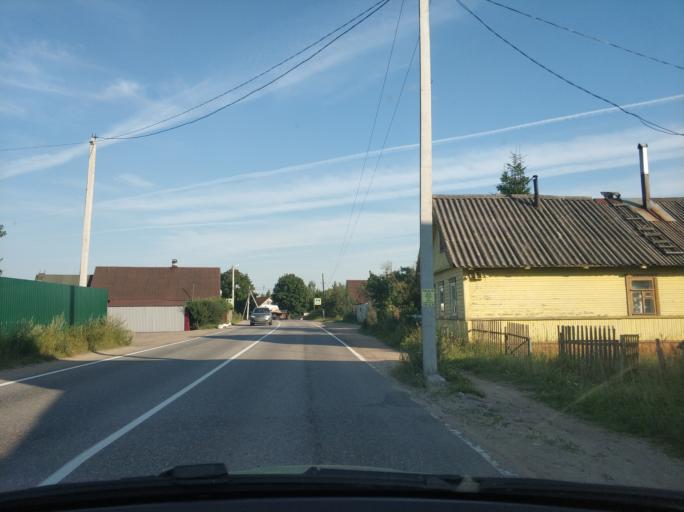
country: RU
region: Leningrad
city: Borisova Griva
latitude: 60.0860
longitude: 31.0236
